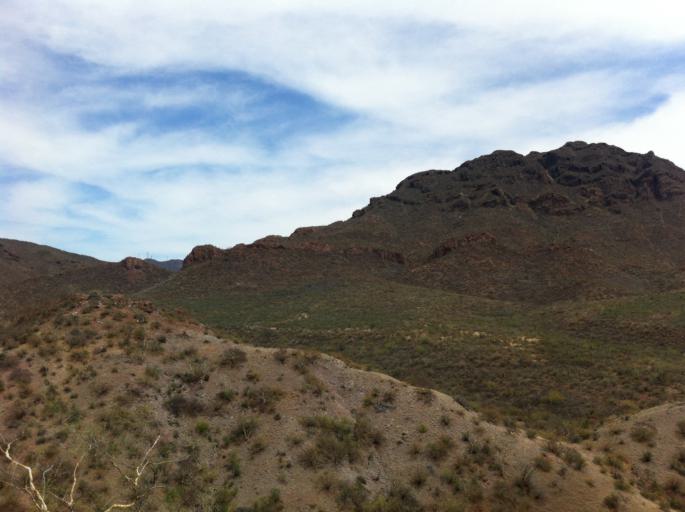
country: MX
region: Sonora
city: Heroica Guaymas
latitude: 27.9494
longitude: -110.9718
